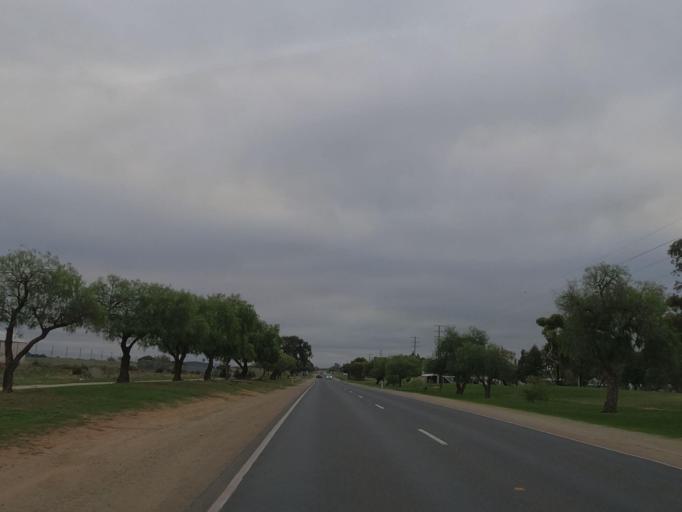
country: AU
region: Victoria
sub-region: Swan Hill
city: Swan Hill
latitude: -35.4552
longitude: 143.6283
